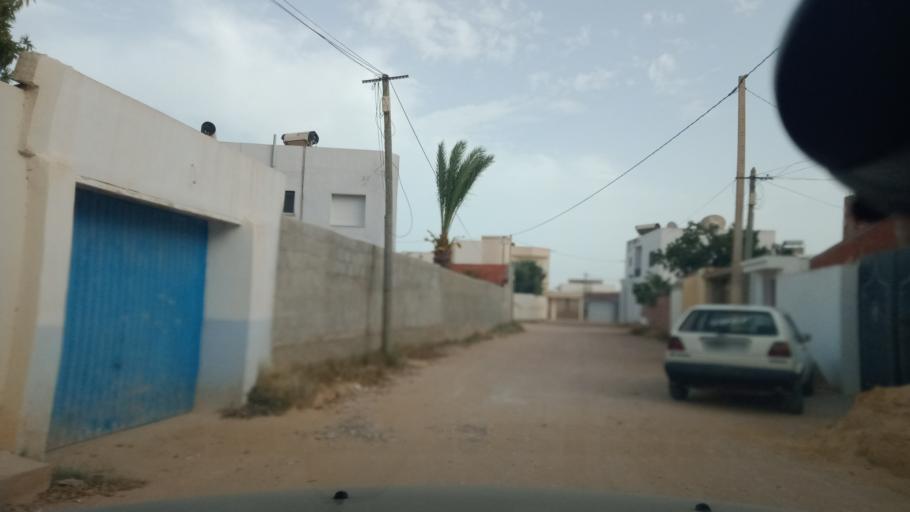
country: TN
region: Safaqis
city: Al Qarmadah
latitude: 34.7862
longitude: 10.7656
